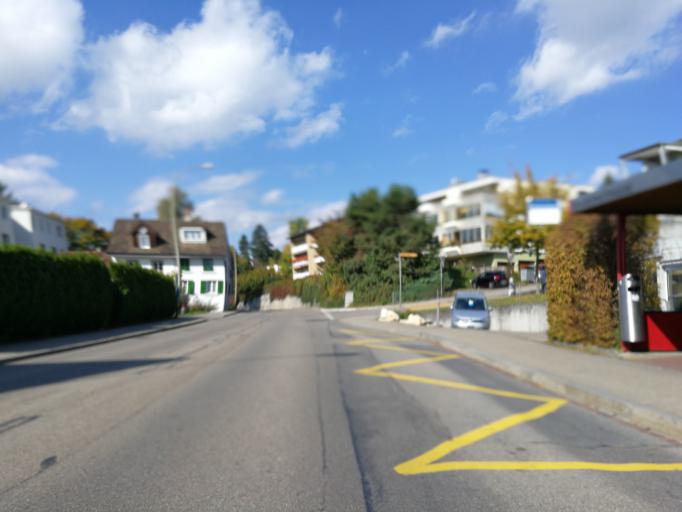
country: CH
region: Zurich
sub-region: Bezirk Meilen
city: Mannedorf
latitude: 47.2589
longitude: 8.6996
